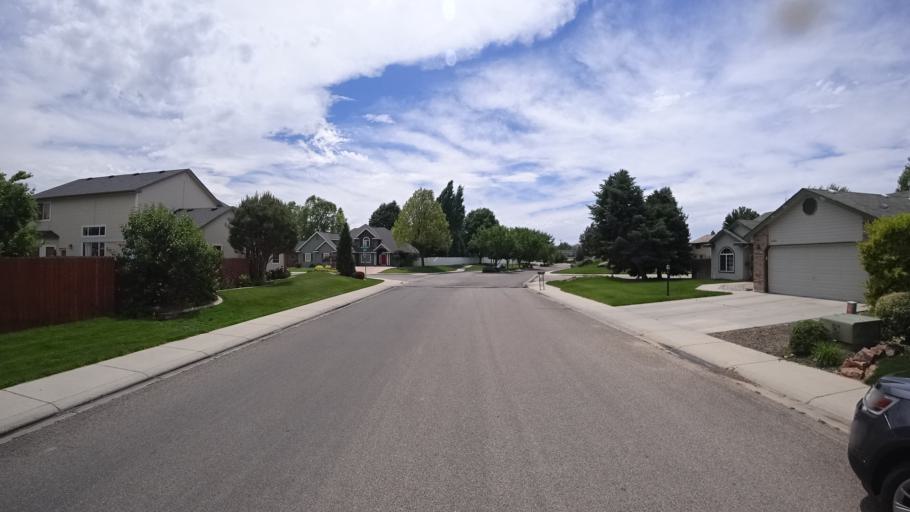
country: US
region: Idaho
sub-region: Ada County
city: Meridian
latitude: 43.6247
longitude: -116.3239
